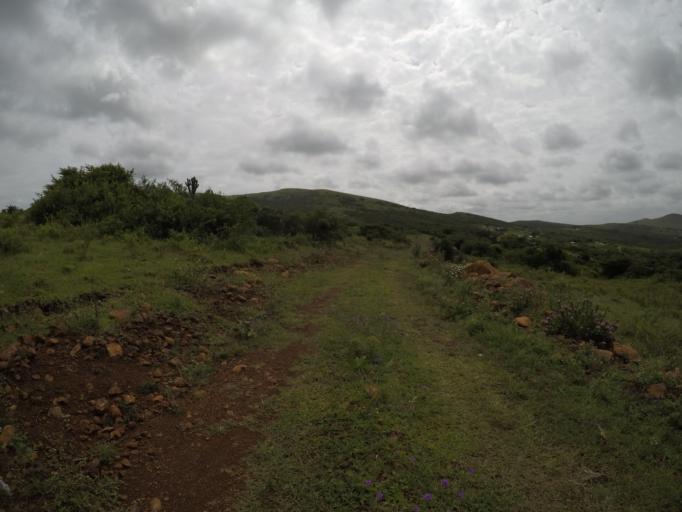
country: ZA
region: KwaZulu-Natal
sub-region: uThungulu District Municipality
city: Empangeni
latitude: -28.6137
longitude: 31.8997
